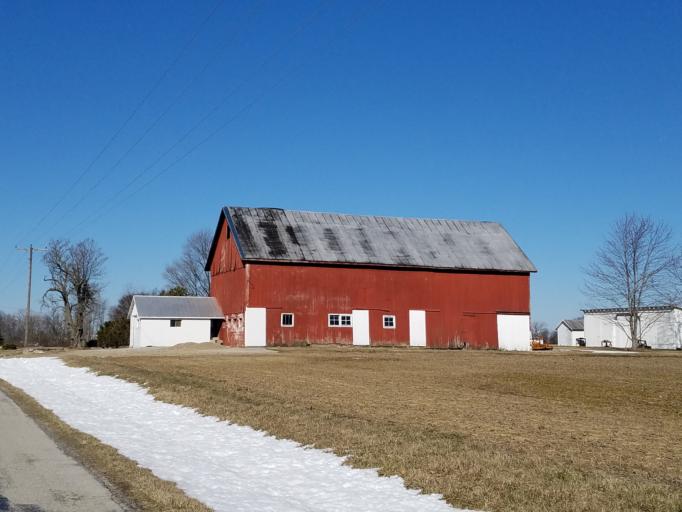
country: US
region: Ohio
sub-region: Crawford County
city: Galion
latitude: 40.6754
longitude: -82.8910
